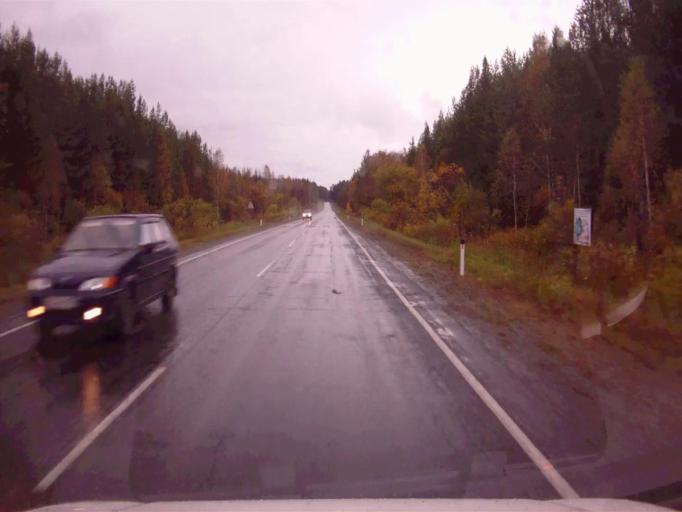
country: RU
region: Chelyabinsk
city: Verkhniy Ufaley
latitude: 56.0159
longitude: 60.3096
